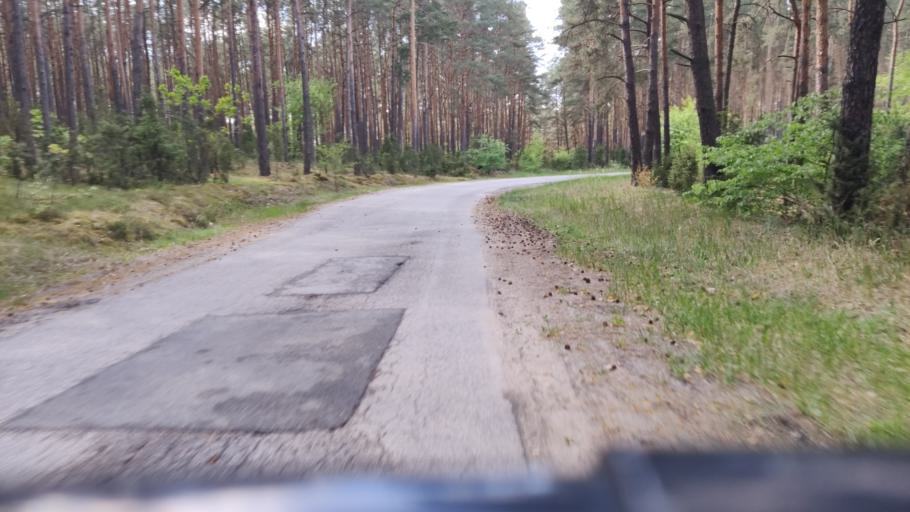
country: PL
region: Kujawsko-Pomorskie
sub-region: Wloclawek
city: Wloclawek
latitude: 52.5972
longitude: 19.0839
